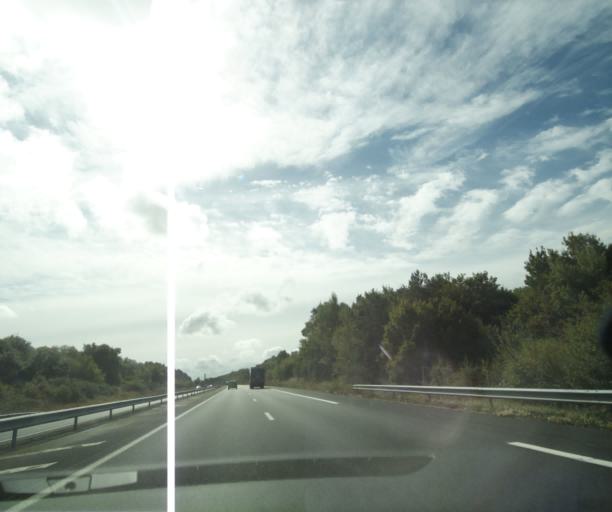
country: FR
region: Poitou-Charentes
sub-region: Departement de la Charente-Maritime
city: Thenac
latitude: 45.6464
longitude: -0.6307
